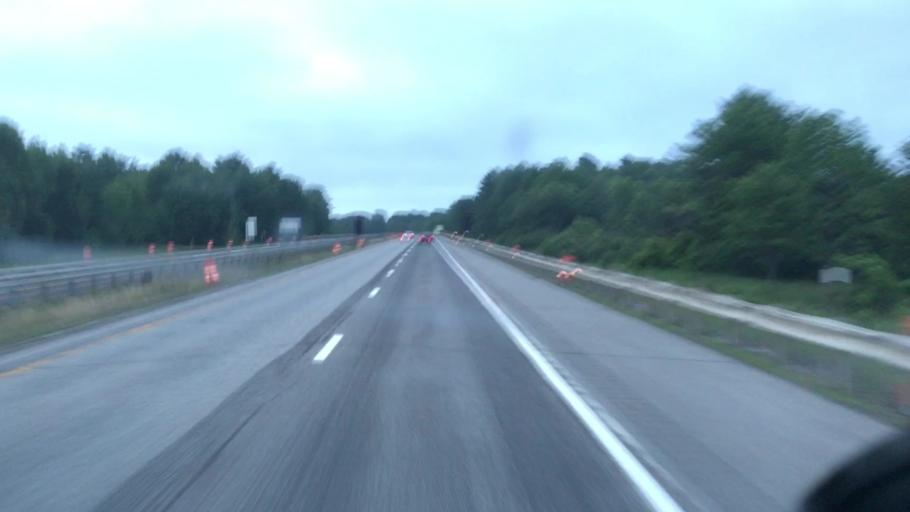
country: US
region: Maine
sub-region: Androscoggin County
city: Auburn
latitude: 44.0549
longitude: -70.2214
